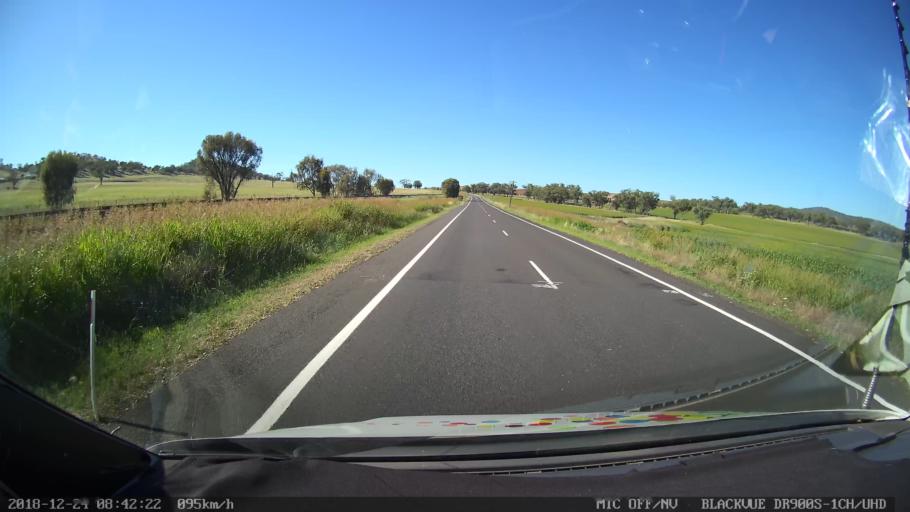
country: AU
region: New South Wales
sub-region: Liverpool Plains
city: Quirindi
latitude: -31.3738
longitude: 150.6431
